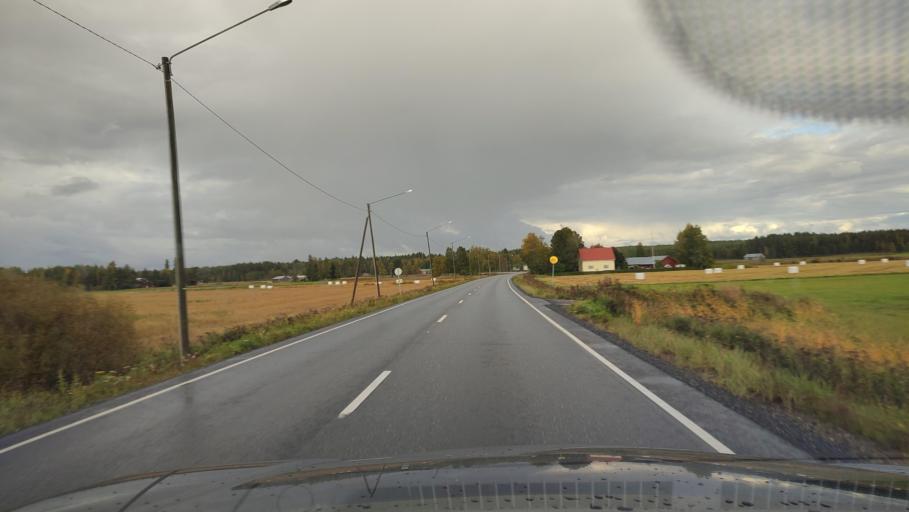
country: FI
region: Southern Ostrobothnia
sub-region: Suupohja
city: Karijoki
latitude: 62.2674
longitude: 21.5505
